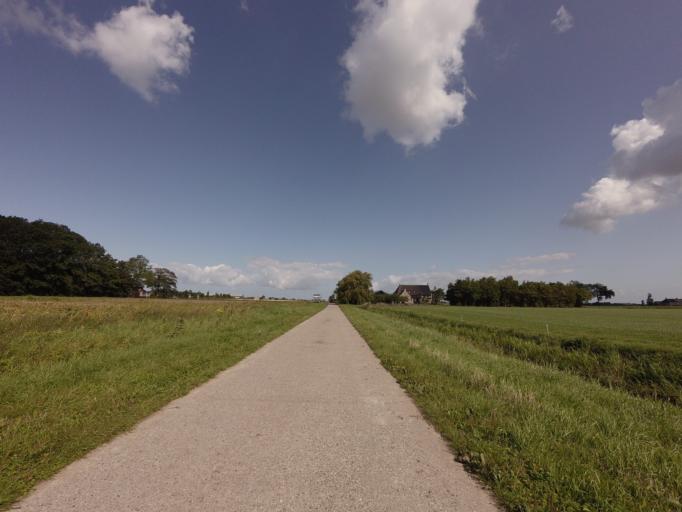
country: NL
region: Friesland
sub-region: Gemeente Het Bildt
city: Sint Jacobiparochie
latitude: 53.2720
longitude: 5.6155
